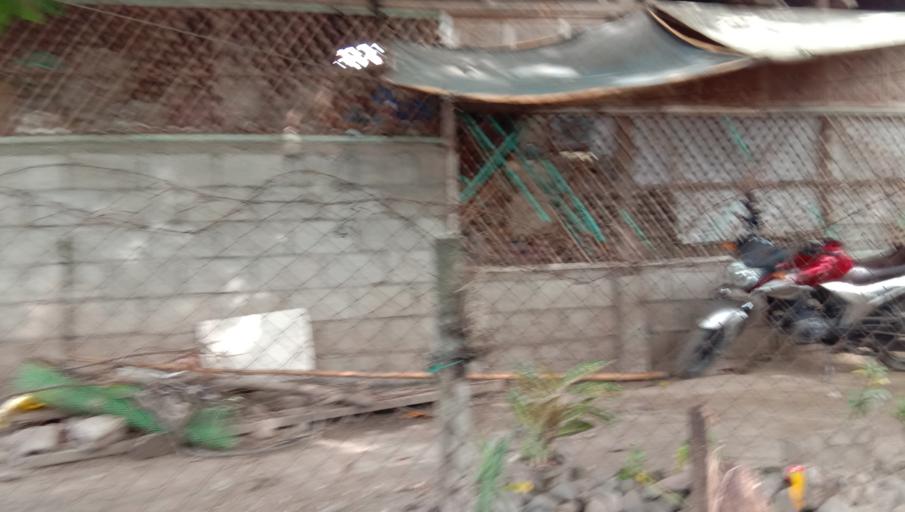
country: PH
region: Central Visayas
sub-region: Province of Negros Oriental
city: Dumaguete
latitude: 9.3022
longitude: 123.3013
